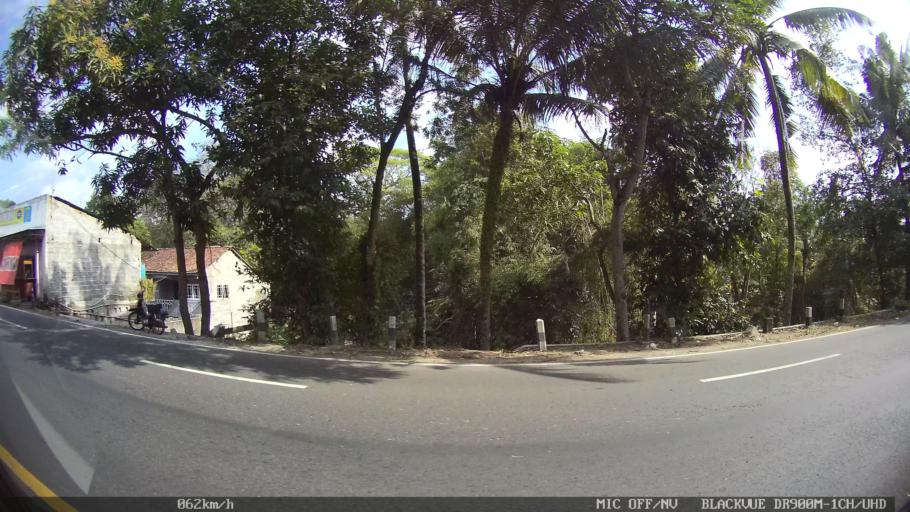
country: ID
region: Daerah Istimewa Yogyakarta
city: Godean
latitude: -7.8156
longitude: 110.2513
